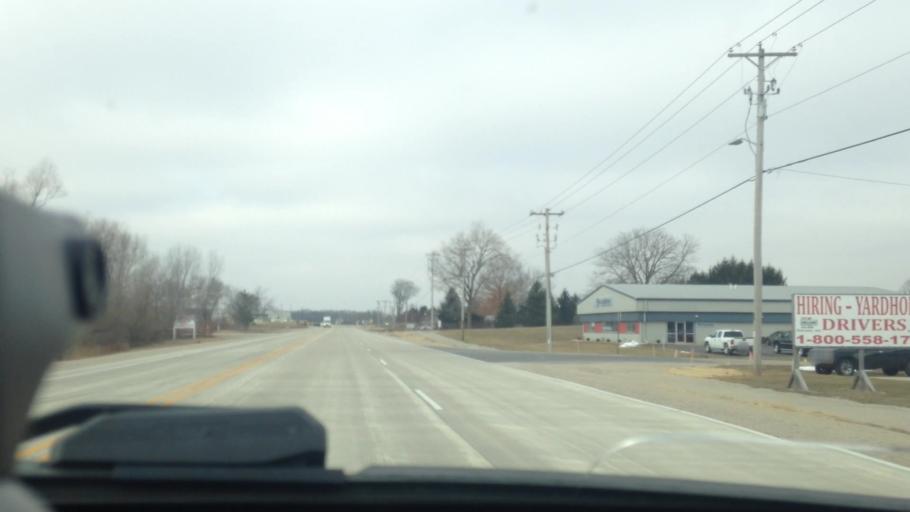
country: US
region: Wisconsin
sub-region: Dodge County
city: Horicon
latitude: 43.4535
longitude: -88.6493
